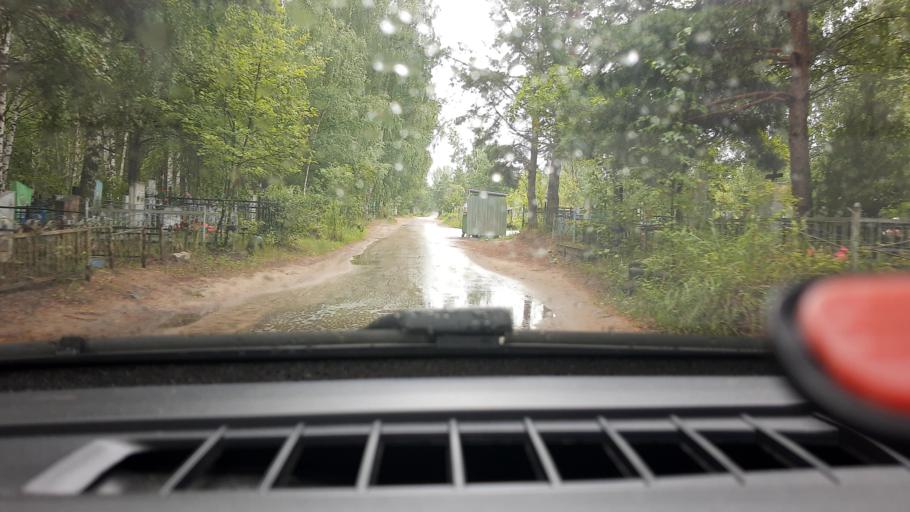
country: RU
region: Nizjnij Novgorod
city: Gorbatovka
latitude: 56.3549
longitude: 43.7776
